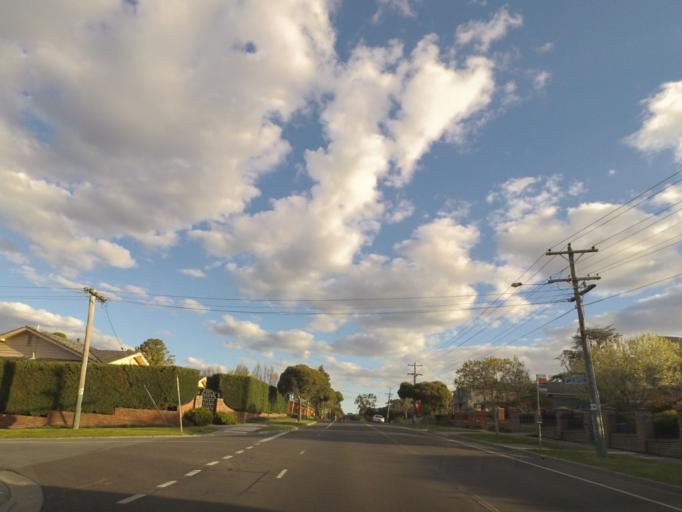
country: AU
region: Victoria
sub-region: Boroondara
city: Balwyn North
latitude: -37.7963
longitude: 145.0986
